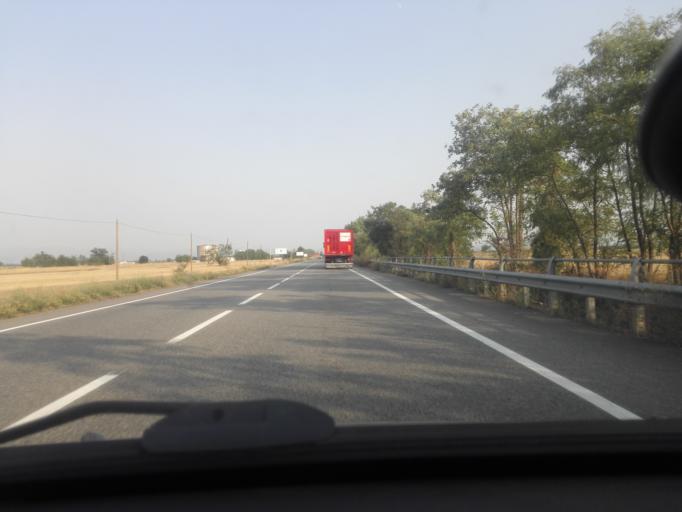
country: IT
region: Piedmont
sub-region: Provincia di Alessandria
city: Litta Parodi-Cascinagrossa
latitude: 44.8639
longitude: 8.7051
